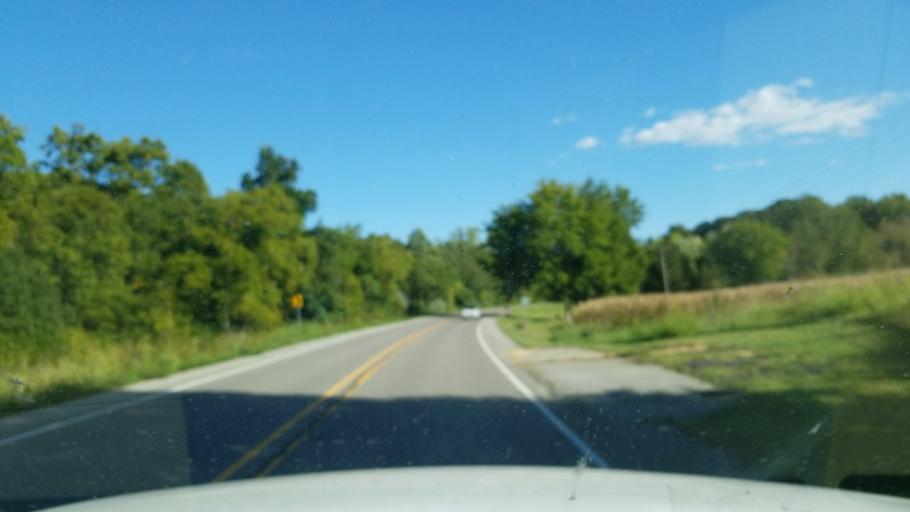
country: US
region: Illinois
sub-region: Saline County
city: Harrisburg
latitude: 37.5946
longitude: -88.4551
